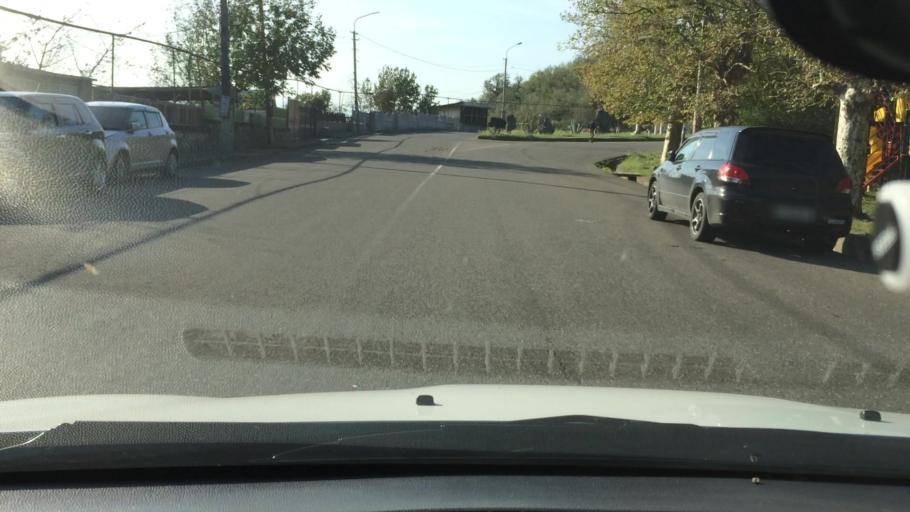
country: GE
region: Imereti
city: Kutaisi
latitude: 42.2638
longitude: 42.7230
